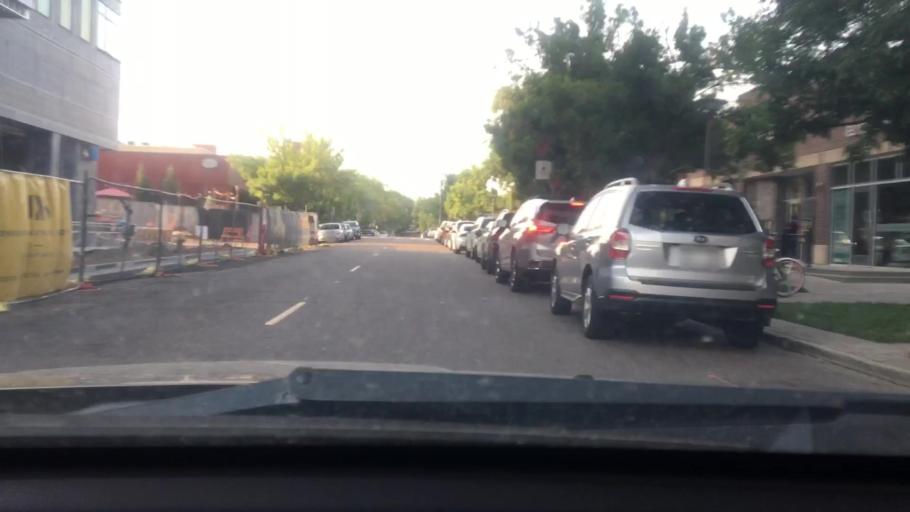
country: US
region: Colorado
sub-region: Arapahoe County
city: Glendale
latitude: 39.7185
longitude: -104.9498
